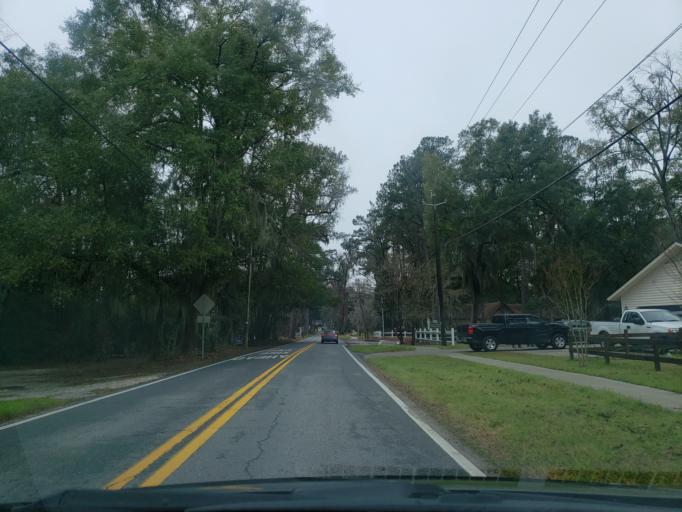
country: US
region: Georgia
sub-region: Chatham County
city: Montgomery
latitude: 31.9435
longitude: -81.1488
